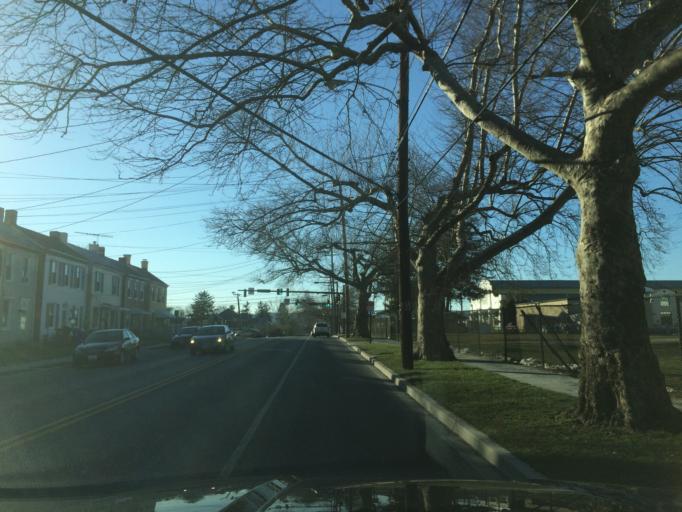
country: US
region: Maryland
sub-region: Frederick County
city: Frederick
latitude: 39.4101
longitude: -77.3933
